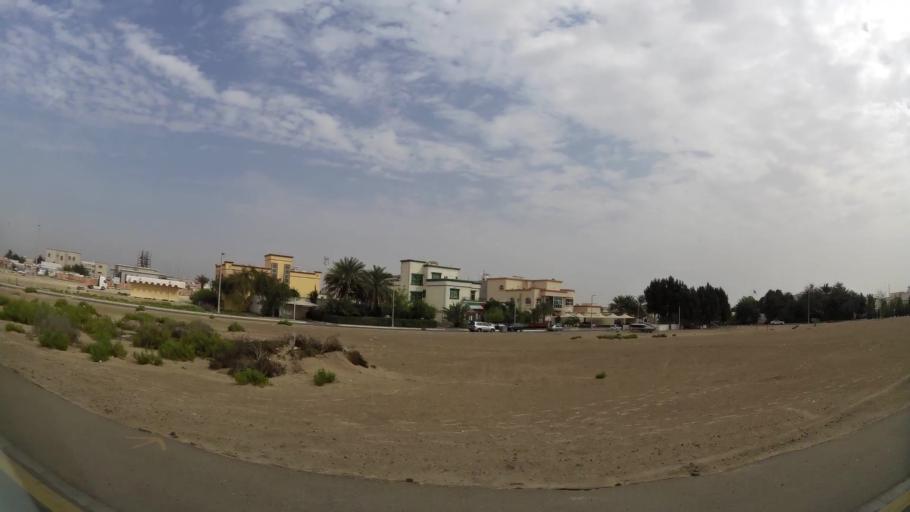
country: AE
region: Abu Dhabi
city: Abu Dhabi
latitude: 24.3154
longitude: 54.6361
